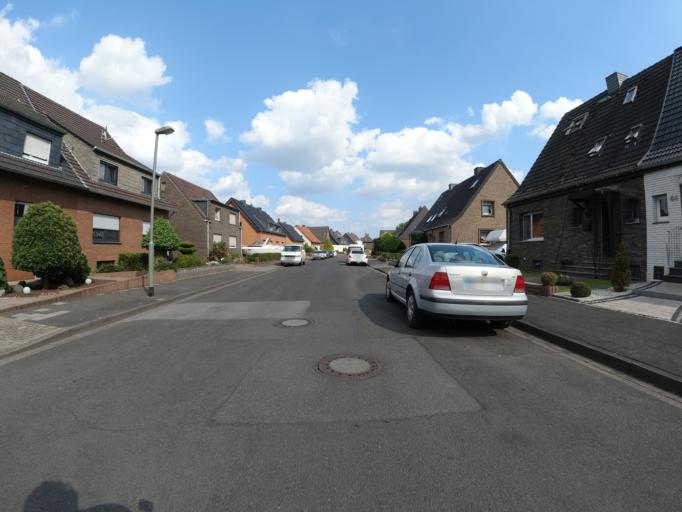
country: DE
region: North Rhine-Westphalia
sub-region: Regierungsbezirk Dusseldorf
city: Moers
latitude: 51.3962
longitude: 6.6799
